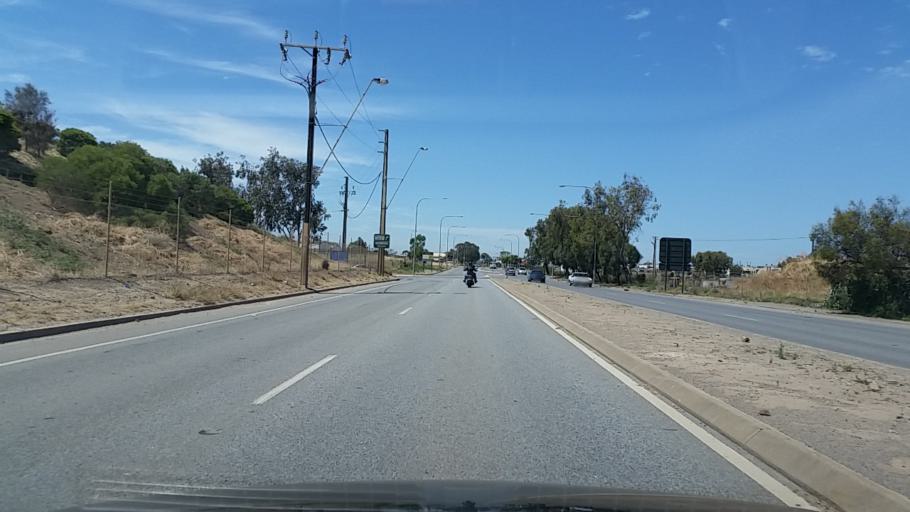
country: AU
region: South Australia
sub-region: Port Adelaide Enfield
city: Alberton
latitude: -34.8359
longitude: 138.5458
